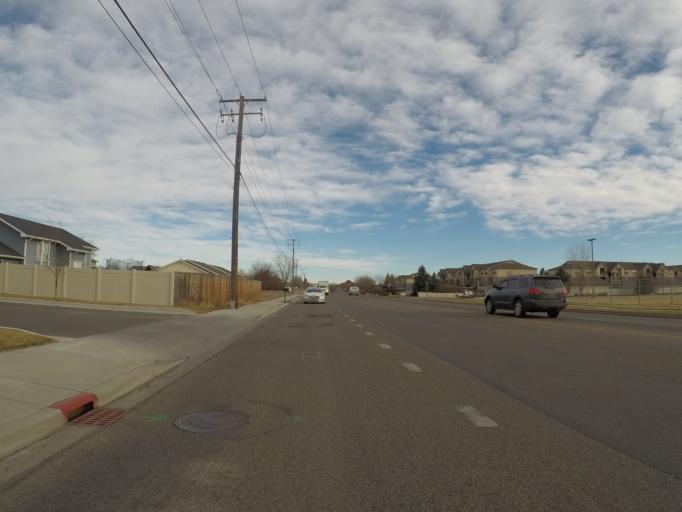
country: US
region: Montana
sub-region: Yellowstone County
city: Billings
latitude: 45.7697
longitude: -108.5953
